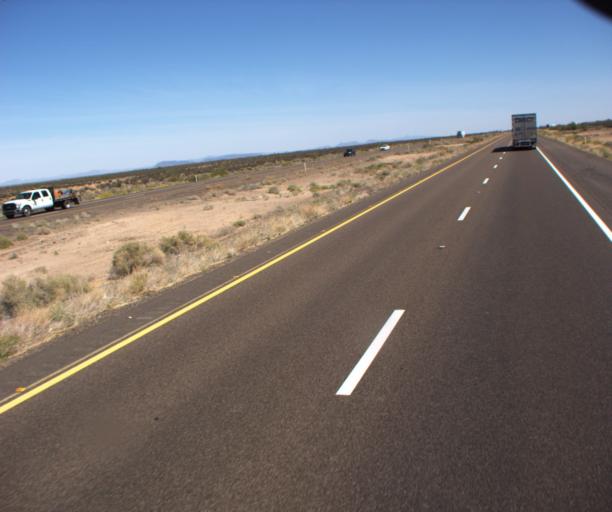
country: US
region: Arizona
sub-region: Yuma County
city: Wellton
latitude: 32.8146
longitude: -113.5034
